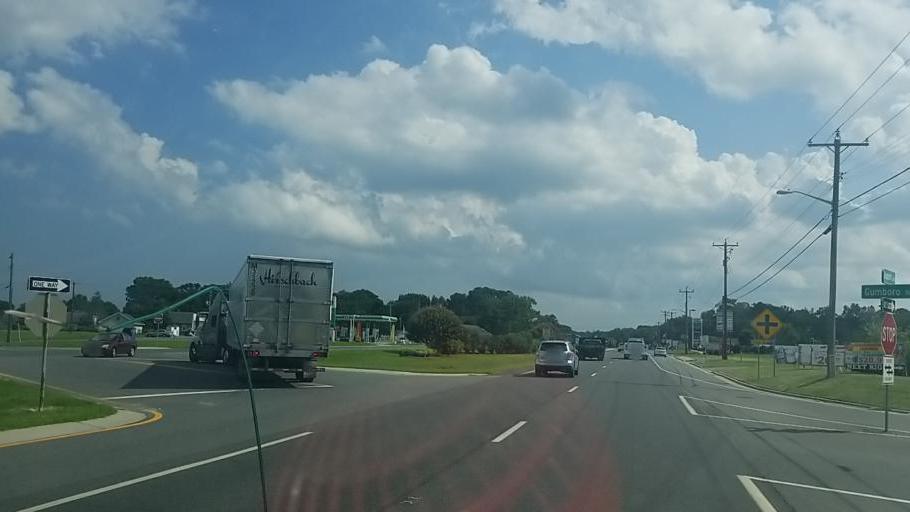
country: US
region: Delaware
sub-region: Sussex County
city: Selbyville
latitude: 38.4580
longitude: -75.2337
